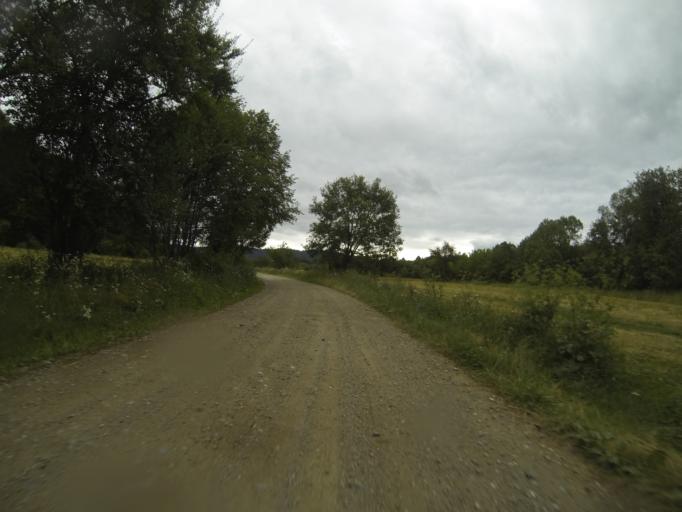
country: RO
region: Brasov
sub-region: Comuna Sinca Noua
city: Sinca Noua
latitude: 45.7153
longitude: 25.2142
